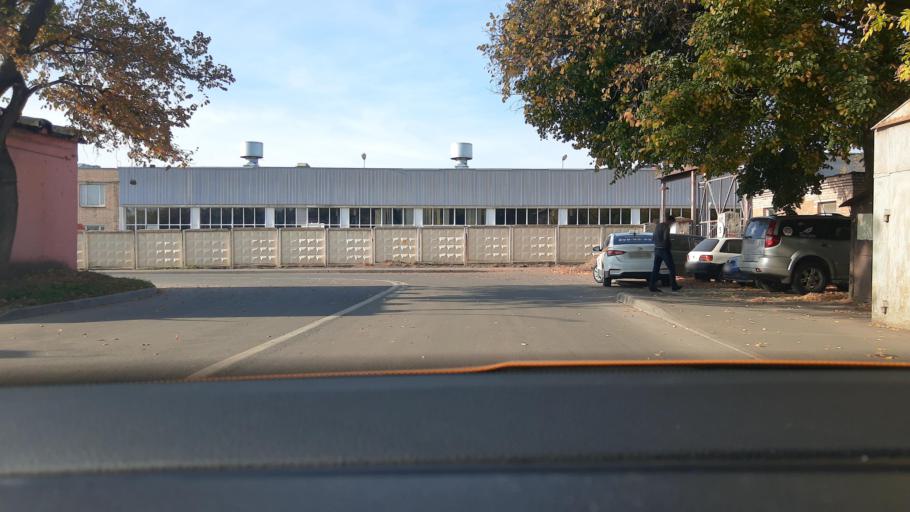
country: RU
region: Moskovskaya
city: Kur'yanovo
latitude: 55.6598
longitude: 37.6999
